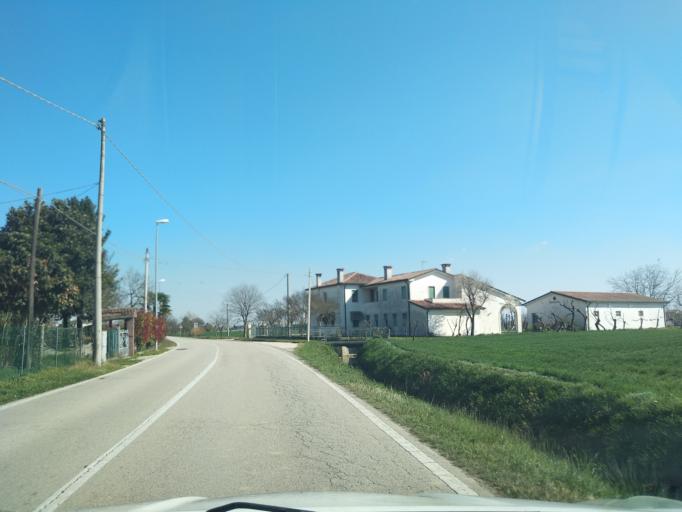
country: IT
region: Veneto
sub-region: Provincia di Padova
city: Villafranca Padovana
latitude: 45.5008
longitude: 11.8054
